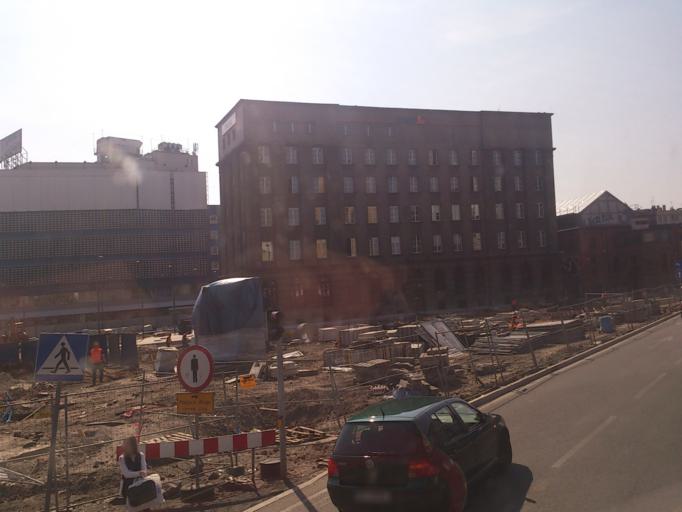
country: PL
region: Silesian Voivodeship
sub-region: Katowice
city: Katowice
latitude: 50.2610
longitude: 19.0223
